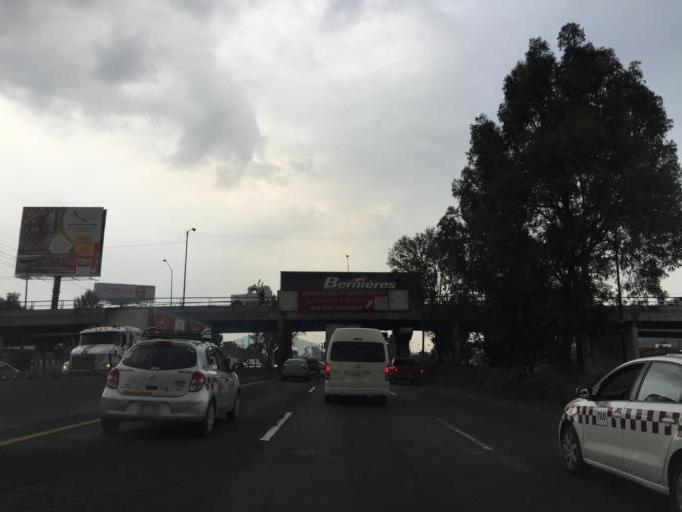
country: MX
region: Mexico
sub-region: Tultitlan
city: Buenavista
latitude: 19.6243
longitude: -99.1925
